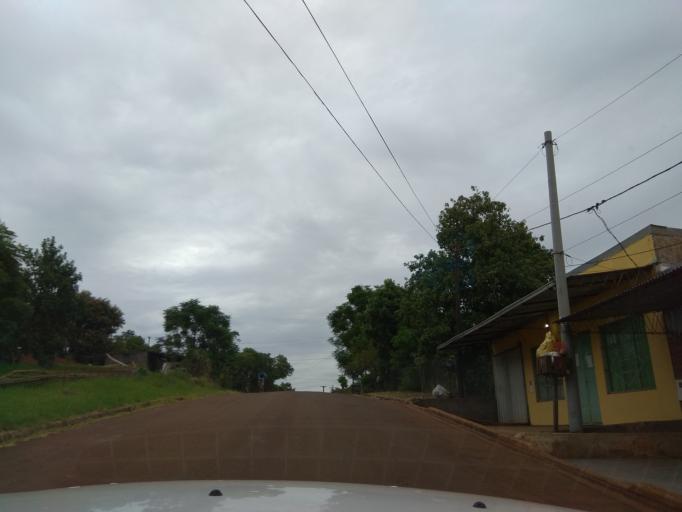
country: AR
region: Misiones
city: Garupa
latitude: -27.4452
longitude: -55.8545
